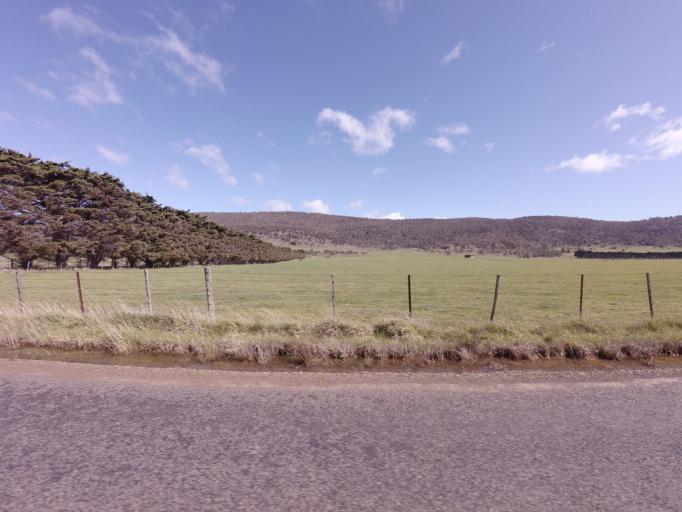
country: AU
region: Tasmania
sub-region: Northern Midlands
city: Evandale
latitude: -41.9658
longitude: 147.4409
